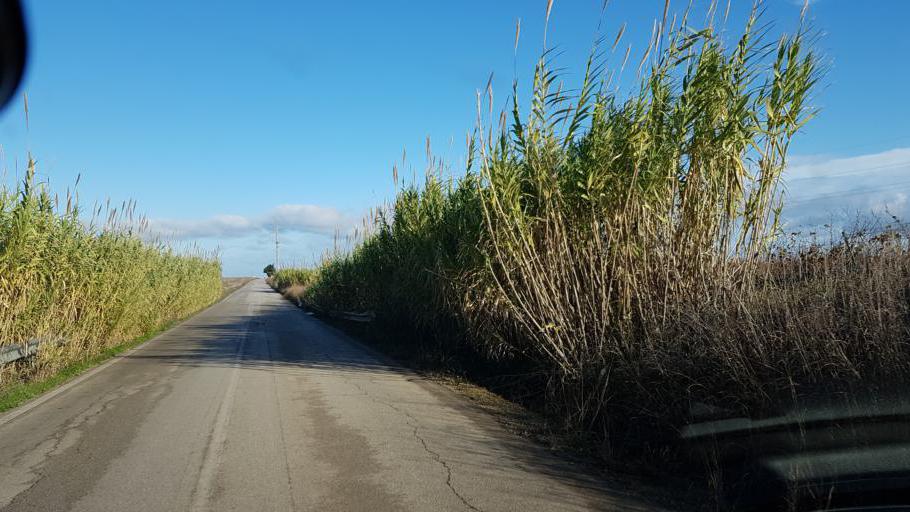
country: IT
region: Apulia
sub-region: Provincia di Brindisi
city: Tuturano
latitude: 40.5690
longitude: 17.9493
